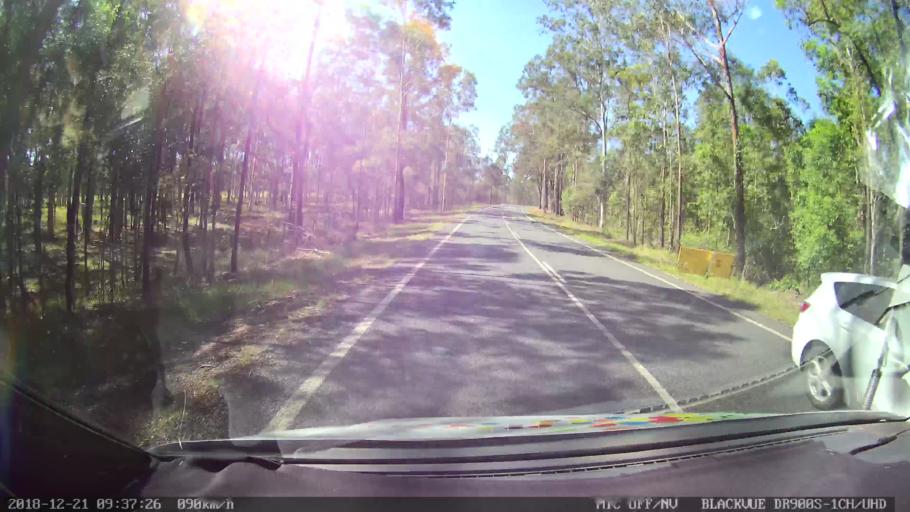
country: AU
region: New South Wales
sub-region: Clarence Valley
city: Grafton
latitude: -29.5362
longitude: 152.9865
